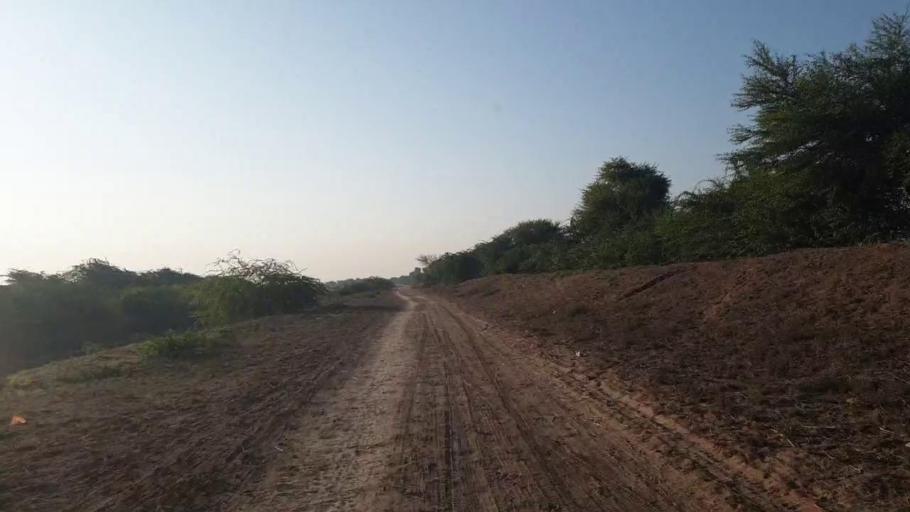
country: PK
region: Sindh
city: Badin
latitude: 24.6426
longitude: 68.7910
